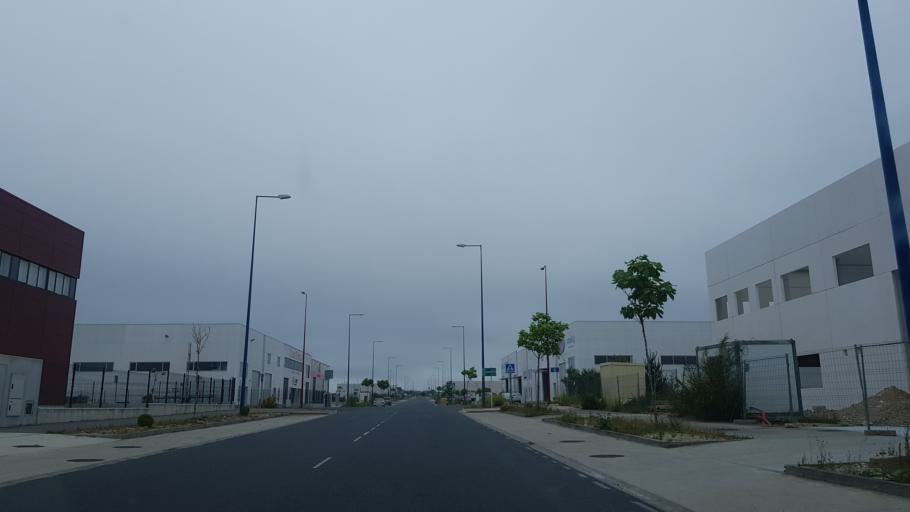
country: ES
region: Galicia
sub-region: Provincia de Lugo
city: Lugo
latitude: 43.0390
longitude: -7.5503
